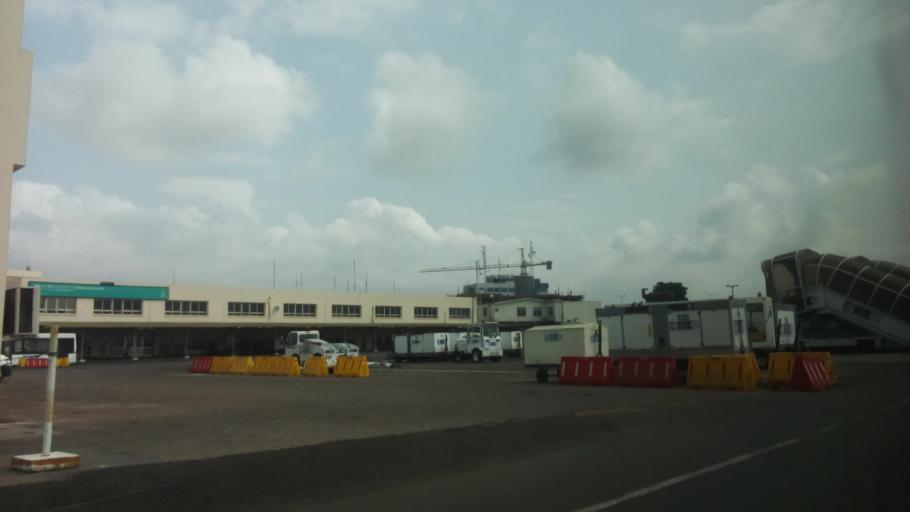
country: GH
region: Greater Accra
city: Accra
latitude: 5.6074
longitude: -0.1704
